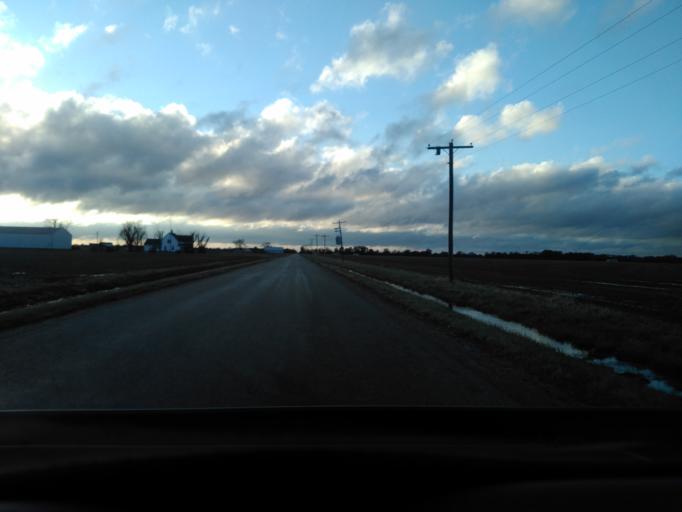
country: US
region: Illinois
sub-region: Effingham County
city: Altamont
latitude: 38.9575
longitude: -88.7350
